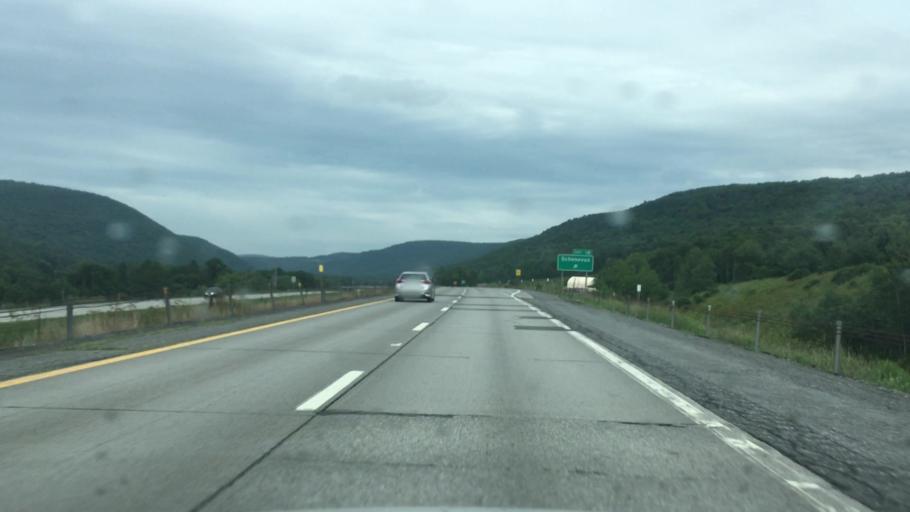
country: US
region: New York
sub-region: Otsego County
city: Worcester
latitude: 42.5408
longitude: -74.8230
